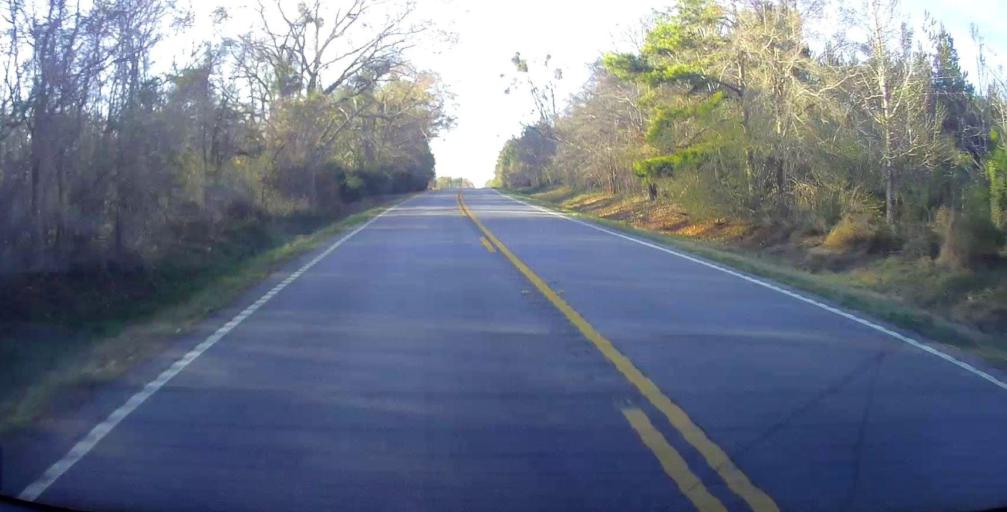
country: US
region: Georgia
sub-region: Wilcox County
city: Abbeville
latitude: 32.1228
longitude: -83.3301
